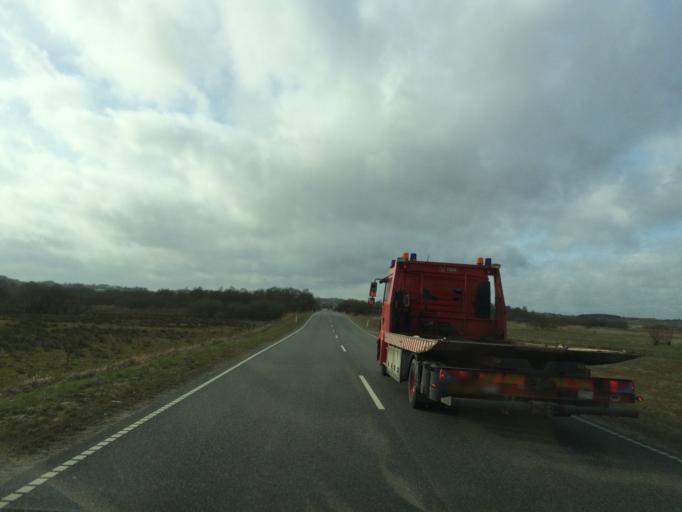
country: DK
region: Central Jutland
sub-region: Randers Kommune
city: Langa
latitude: 56.4874
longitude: 9.8642
